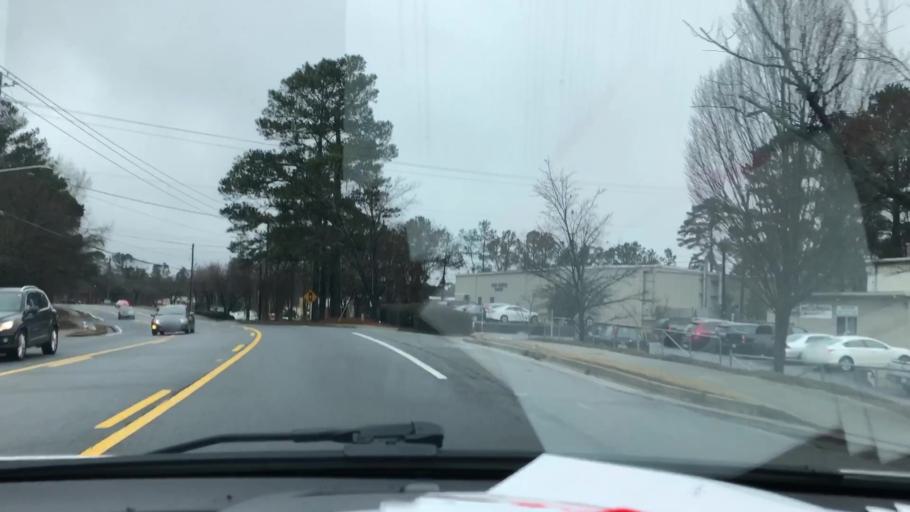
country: US
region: Georgia
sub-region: Gwinnett County
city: Norcross
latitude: 33.9688
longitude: -84.2180
